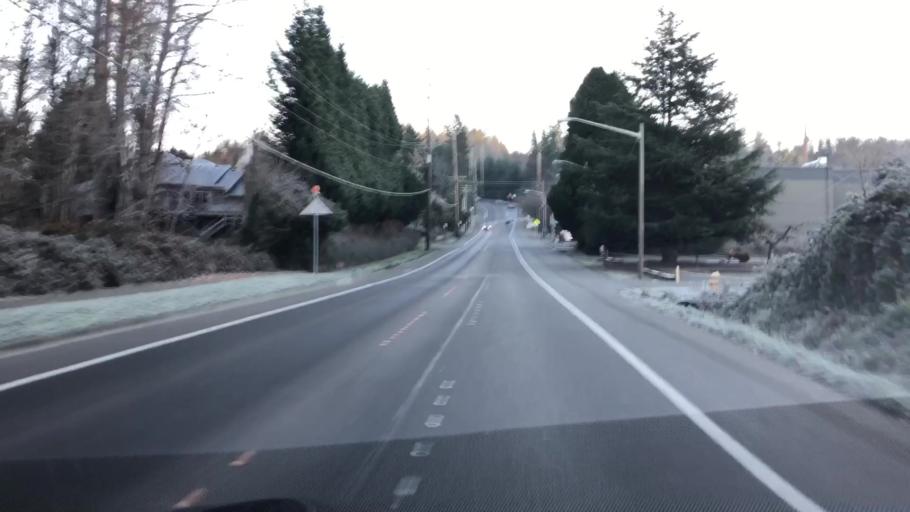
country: US
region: Washington
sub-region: King County
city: Eastgate
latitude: 47.5874
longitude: -122.1607
